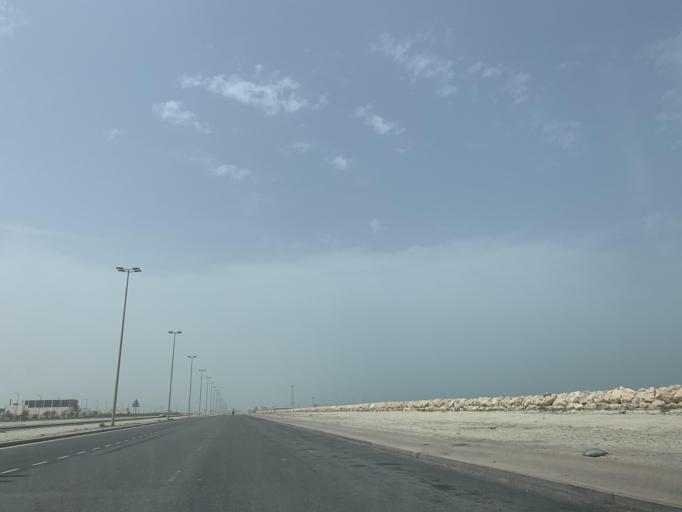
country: BH
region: Muharraq
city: Al Hadd
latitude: 26.2138
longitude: 50.7025
